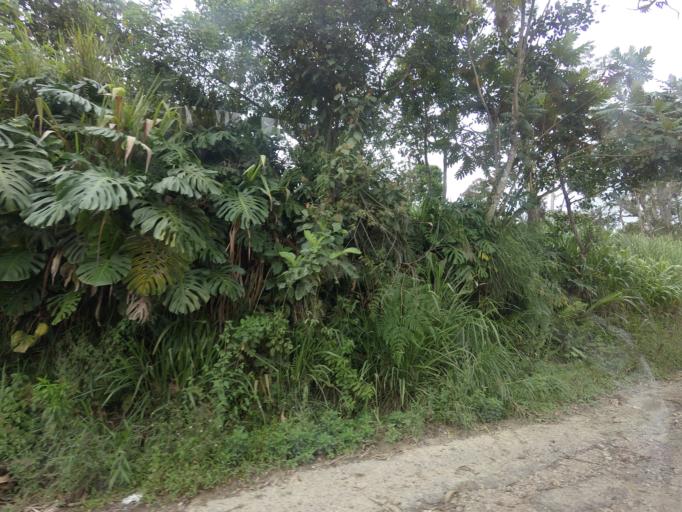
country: CO
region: Huila
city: San Agustin
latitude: 1.9352
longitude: -76.2983
